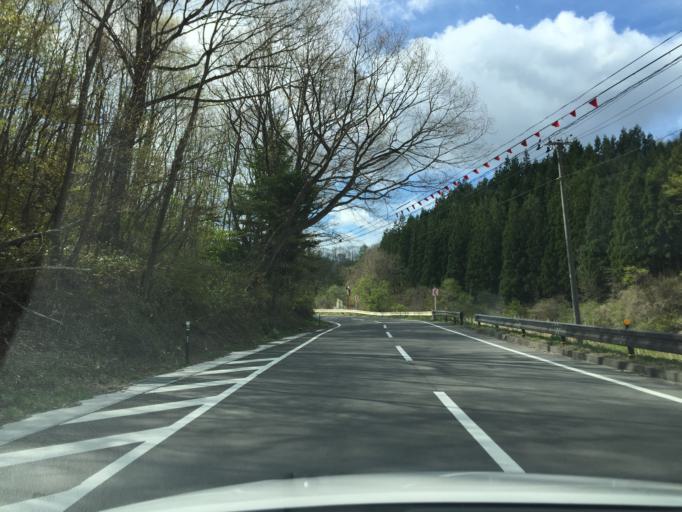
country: JP
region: Fukushima
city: Funehikimachi-funehiki
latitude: 37.6216
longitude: 140.6458
